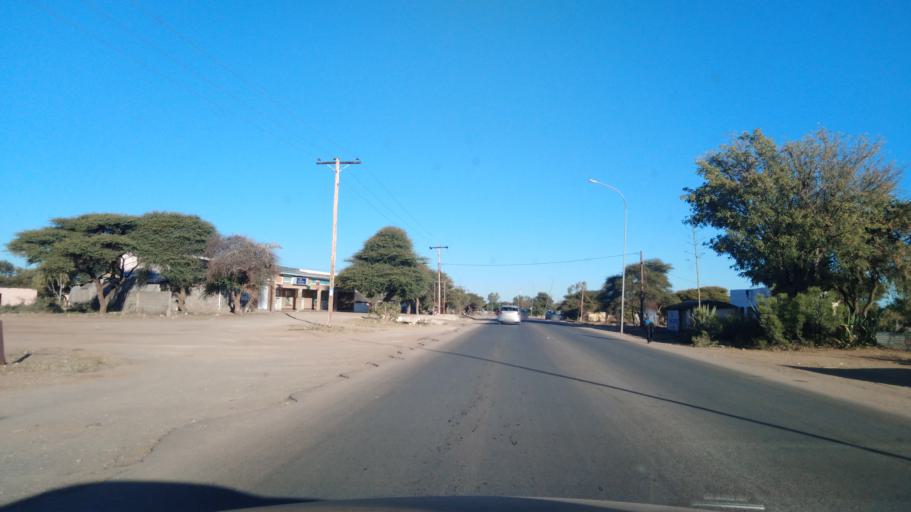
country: BW
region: Central
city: Mahalapye
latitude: -23.1001
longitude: 26.8282
